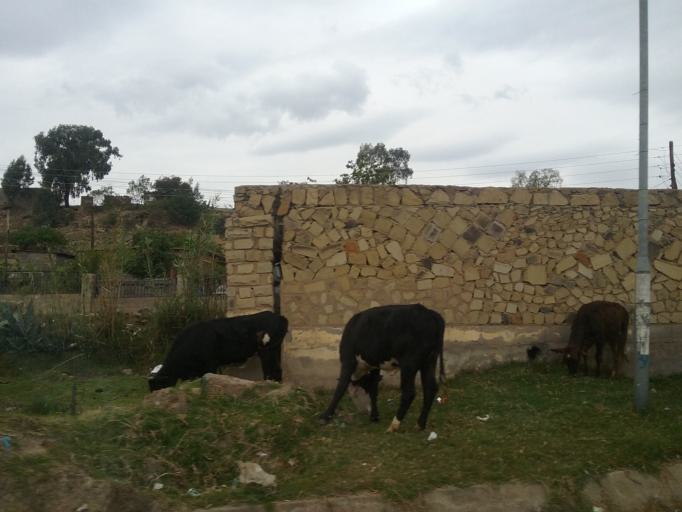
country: LS
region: Maseru
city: Maseru
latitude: -29.3223
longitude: 27.5091
